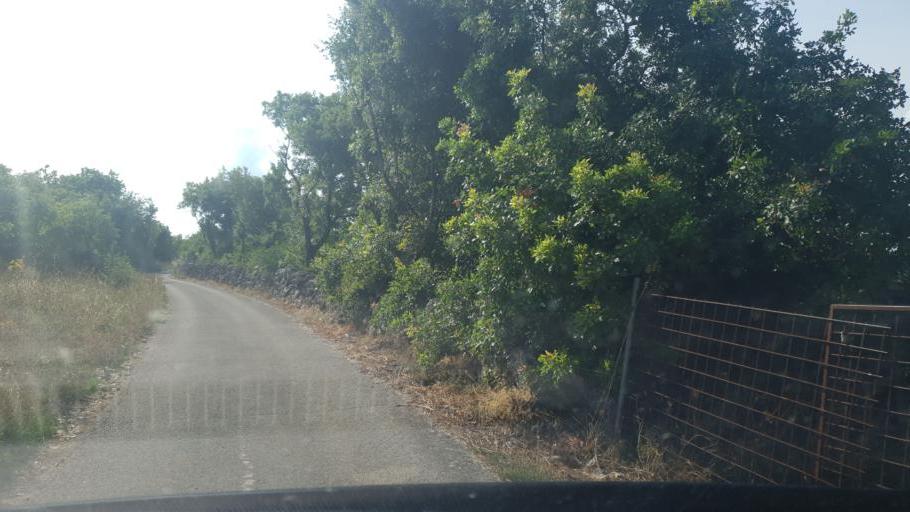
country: HR
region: Primorsko-Goranska
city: Punat
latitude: 45.0757
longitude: 14.6630
